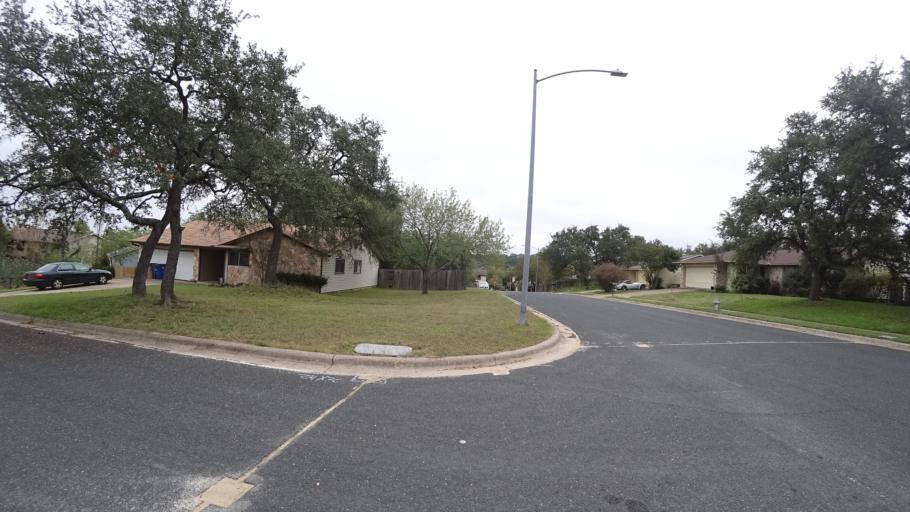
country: US
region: Texas
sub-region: Travis County
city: Barton Creek
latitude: 30.2382
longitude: -97.8942
